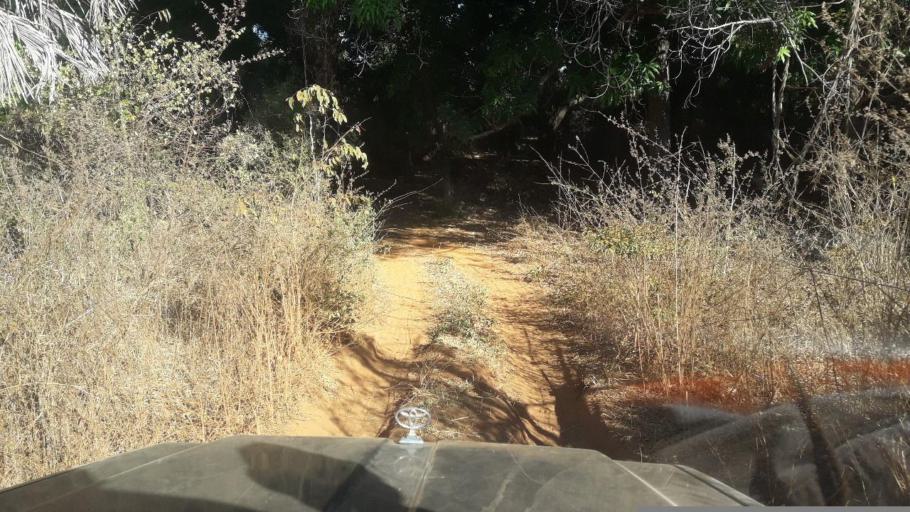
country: MG
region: Boeny
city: Sitampiky
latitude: -16.4060
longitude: 45.5990
